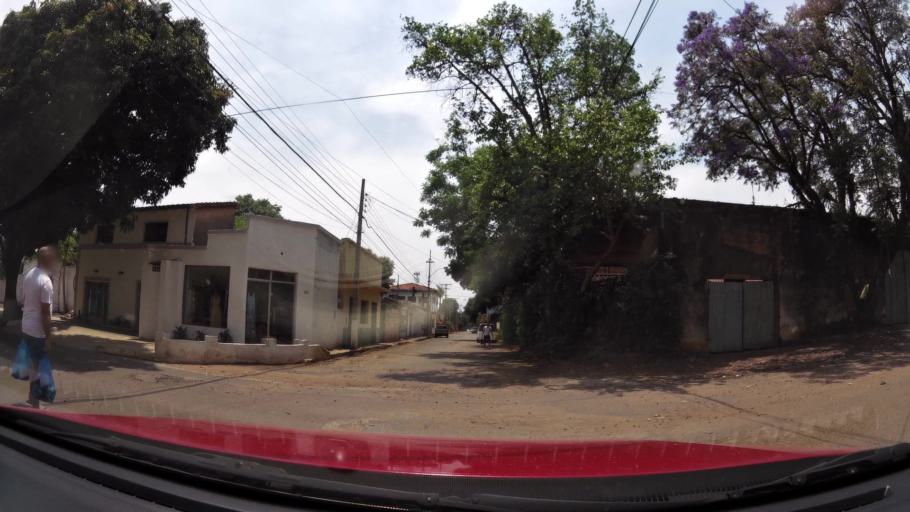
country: PY
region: Central
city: Fernando de la Mora
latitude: -25.3195
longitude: -57.5576
